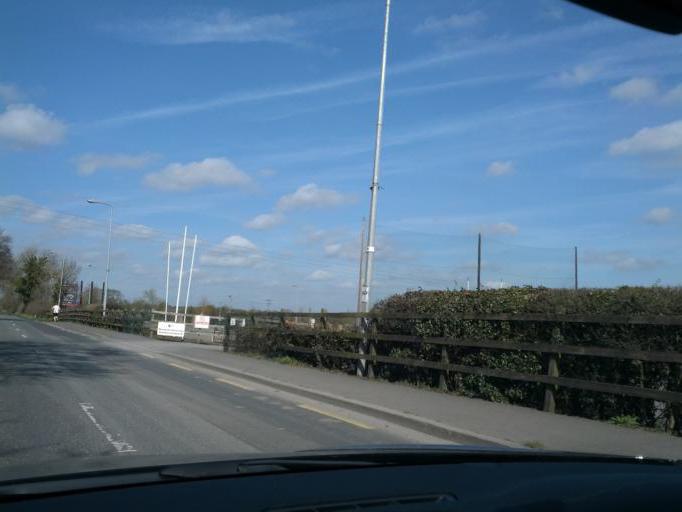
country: IE
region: Leinster
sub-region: Kildare
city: Maynooth
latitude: 53.3921
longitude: -6.5992
